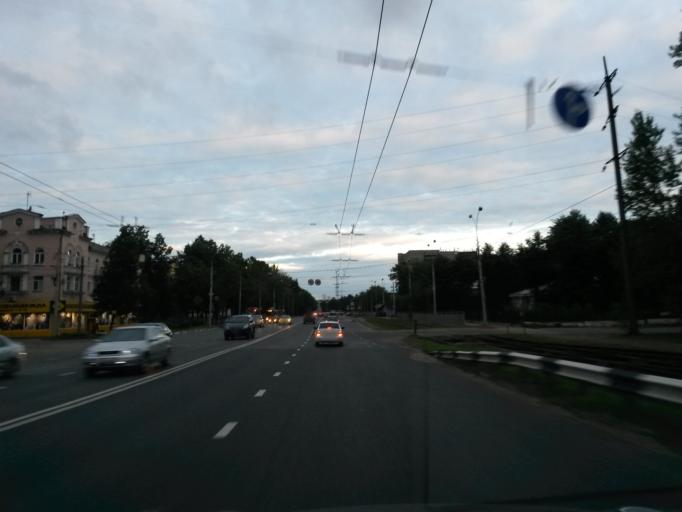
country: RU
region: Jaroslavl
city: Yaroslavl
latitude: 57.6418
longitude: 39.8553
